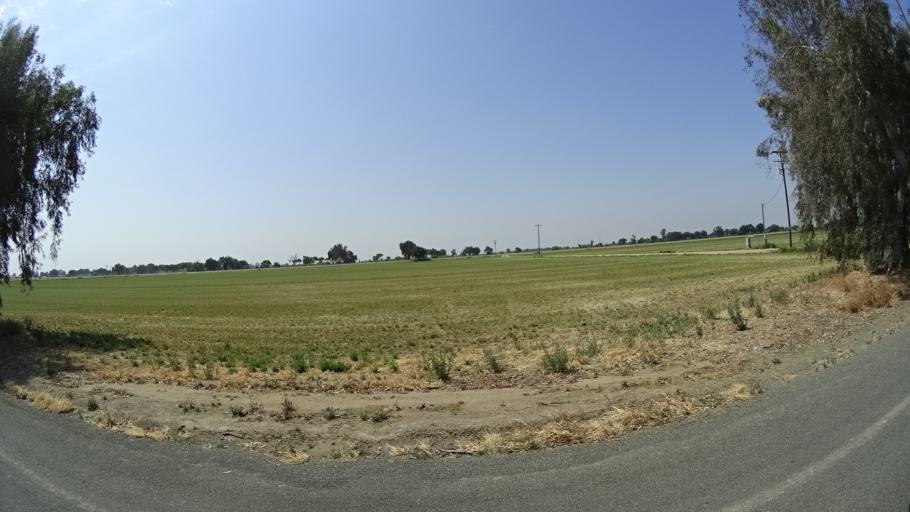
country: US
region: California
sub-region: Fresno County
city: Riverdale
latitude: 36.3948
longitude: -119.7755
